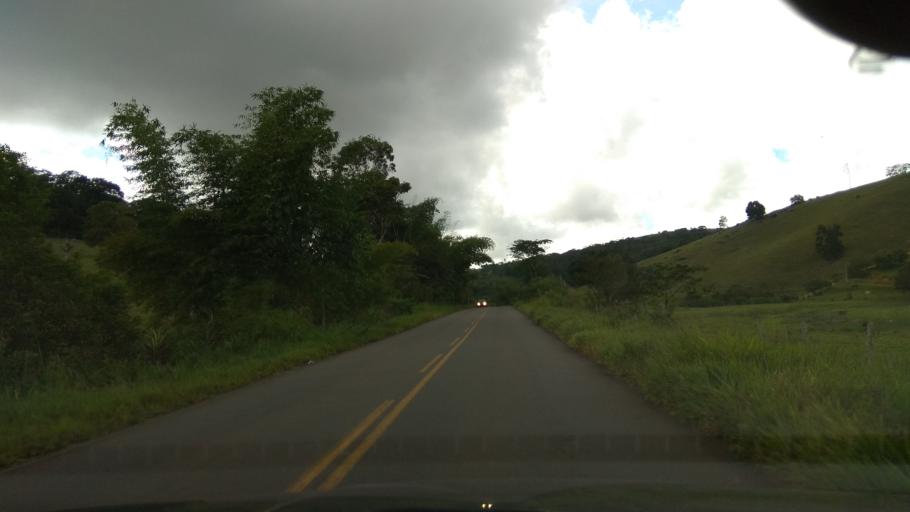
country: BR
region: Bahia
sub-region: Mutuipe
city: Mutuipe
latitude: -13.2485
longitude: -39.5454
